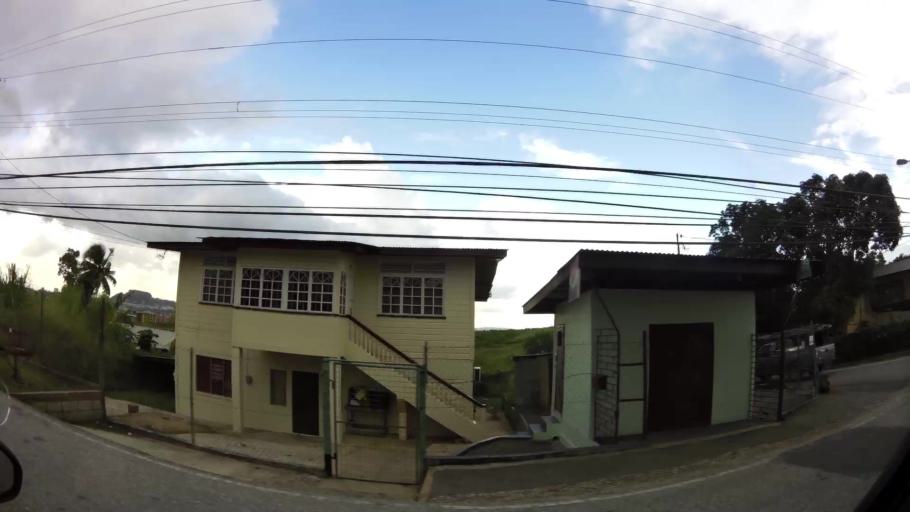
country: TT
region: City of San Fernando
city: Mon Repos
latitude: 10.2452
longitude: -61.4476
